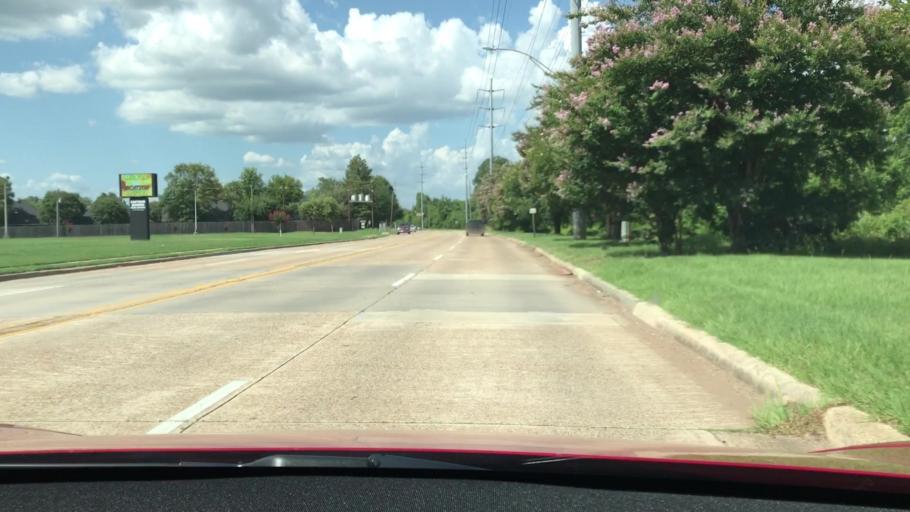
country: US
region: Louisiana
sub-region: Bossier Parish
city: Bossier City
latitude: 32.4476
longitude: -93.7113
